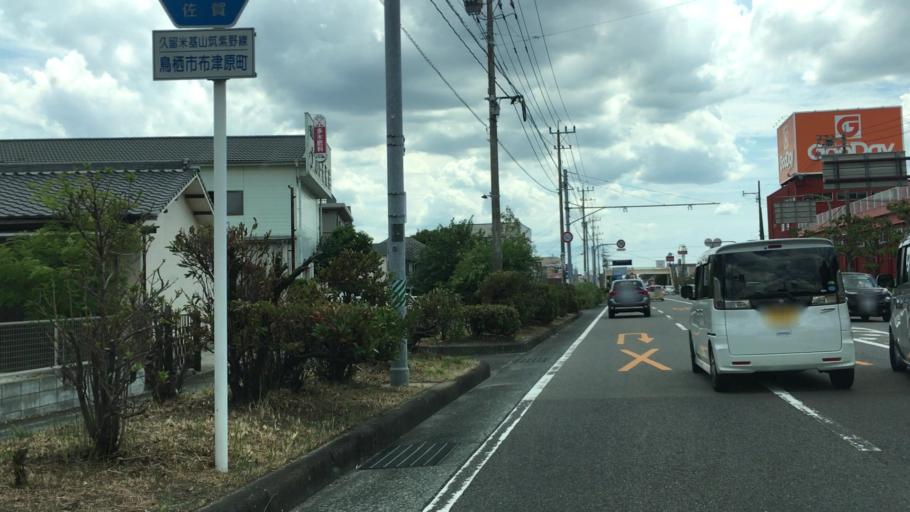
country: JP
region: Saga Prefecture
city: Tosu
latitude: 33.3774
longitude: 130.4989
